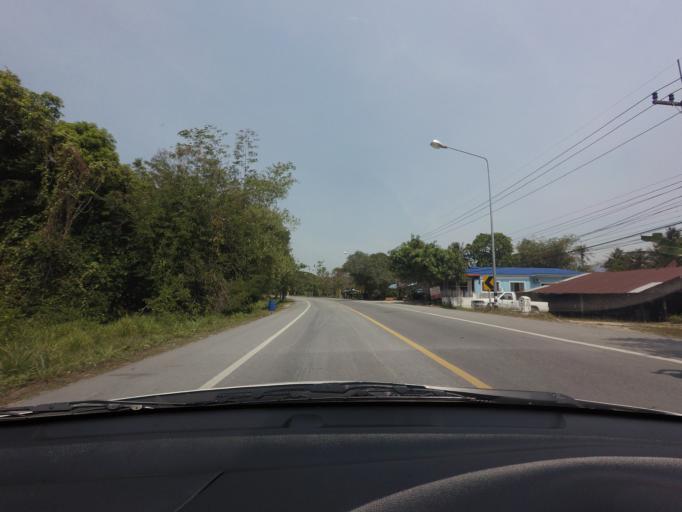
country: TH
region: Chon Buri
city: Si Racha
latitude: 13.2138
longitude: 101.0023
